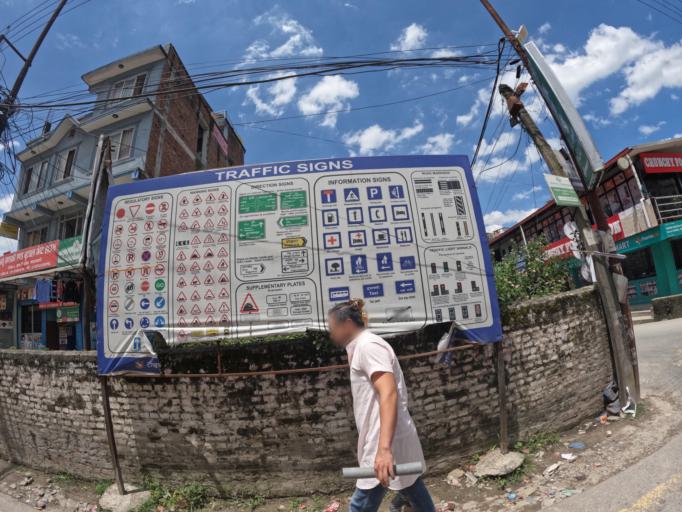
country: NP
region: Central Region
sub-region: Bagmati Zone
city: Kathmandu
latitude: 27.7527
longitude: 85.3269
